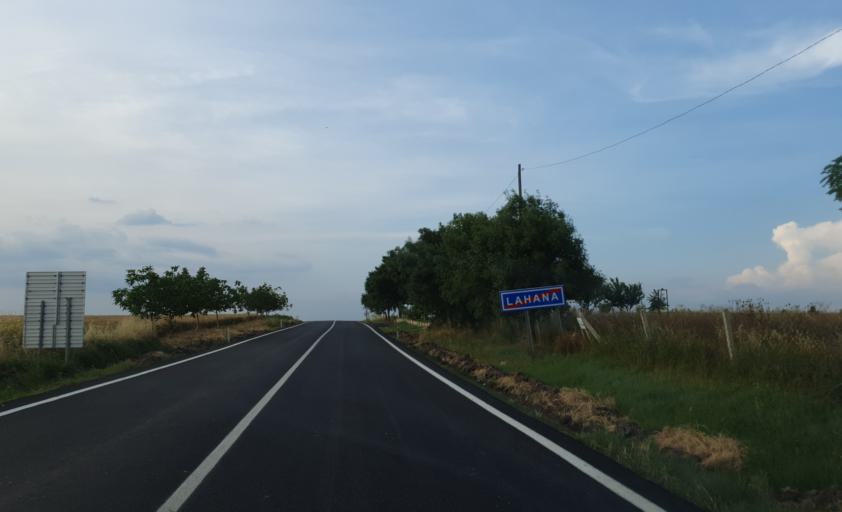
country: TR
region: Tekirdag
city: Hayrabolu
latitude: 41.2953
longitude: 27.1353
